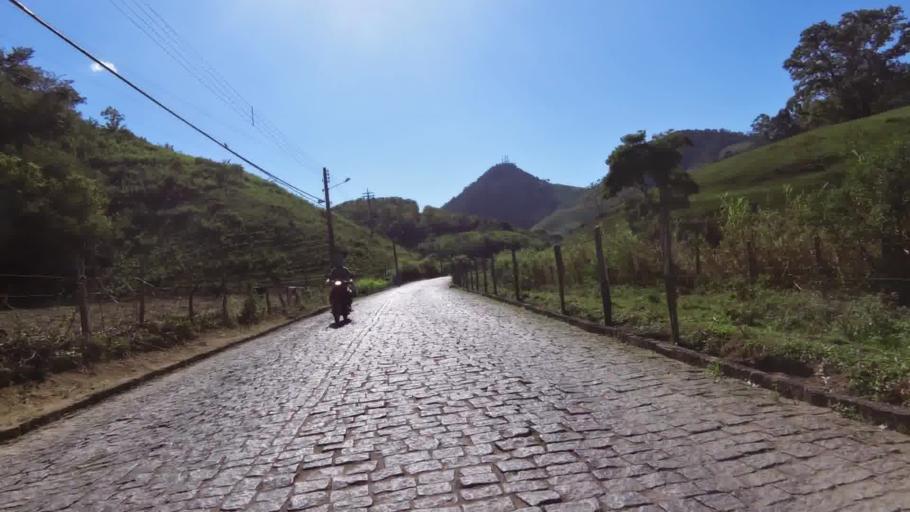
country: BR
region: Espirito Santo
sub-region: Rio Novo Do Sul
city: Rio Novo do Sul
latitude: -20.8560
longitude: -40.9305
